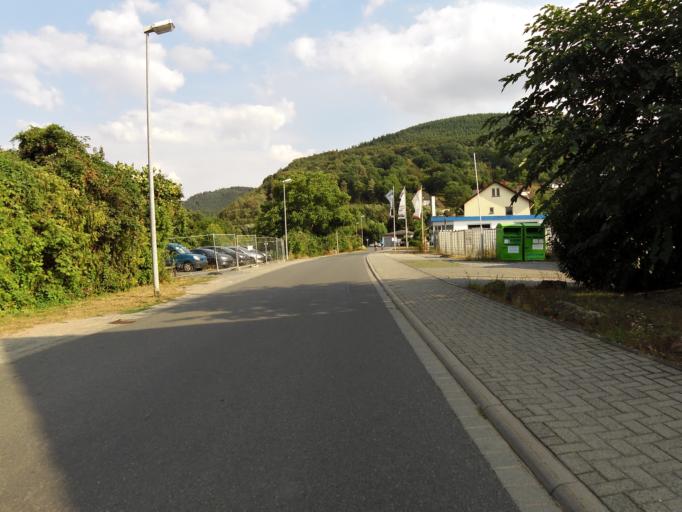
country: DE
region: Bavaria
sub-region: Regierungsbezirk Unterfranken
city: Kleinheubach
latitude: 49.7053
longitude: 9.2326
